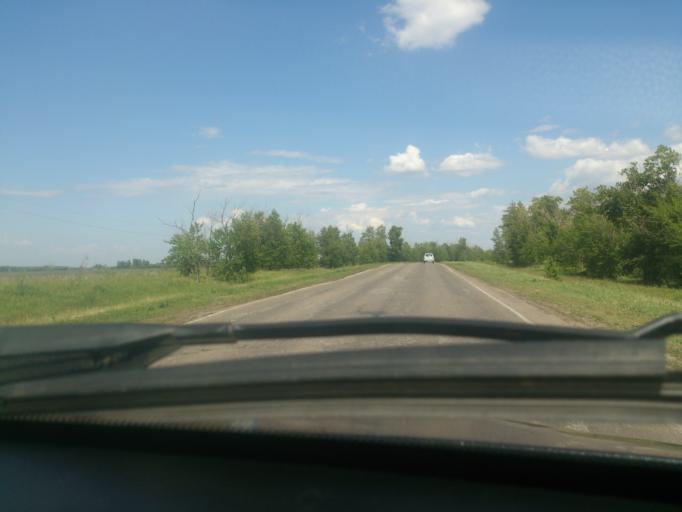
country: RU
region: Ulyanovsk
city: Cherdakly
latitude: 54.3957
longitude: 48.8546
